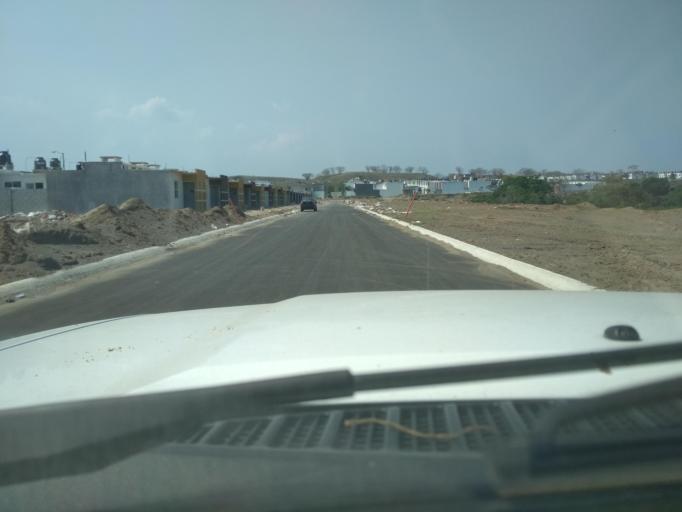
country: MX
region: Veracruz
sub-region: Veracruz
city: Lomas de Rio Medio Cuatro
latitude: 19.1916
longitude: -96.2061
